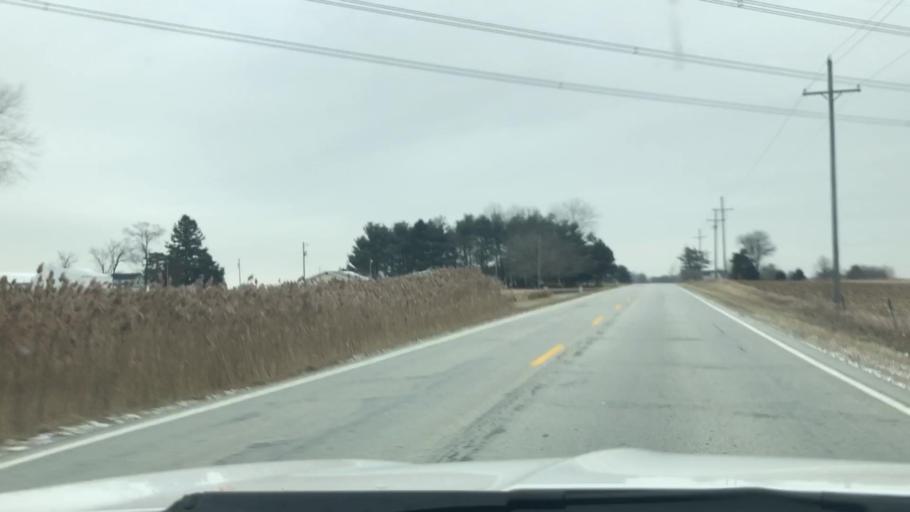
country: US
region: Indiana
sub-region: Fulton County
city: Rochester
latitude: 41.0543
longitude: -86.1425
